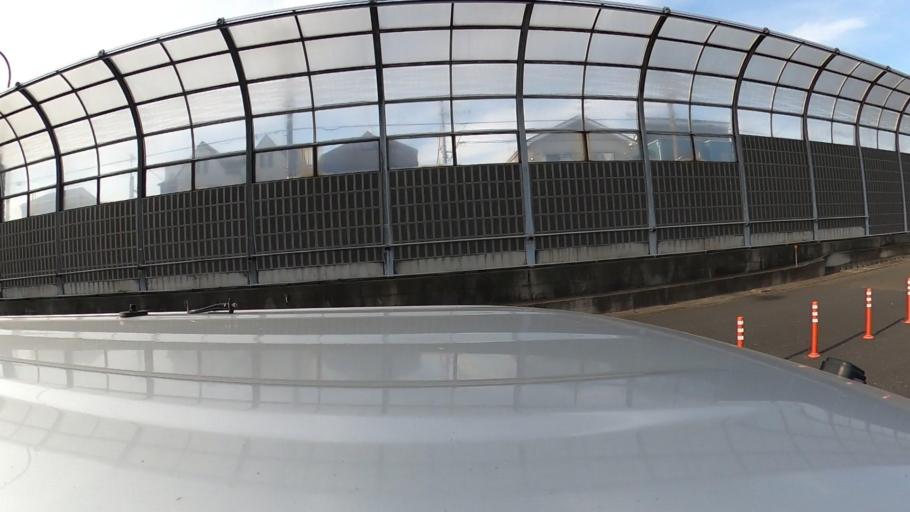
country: JP
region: Saitama
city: Asaka
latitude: 35.7641
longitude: 139.5827
